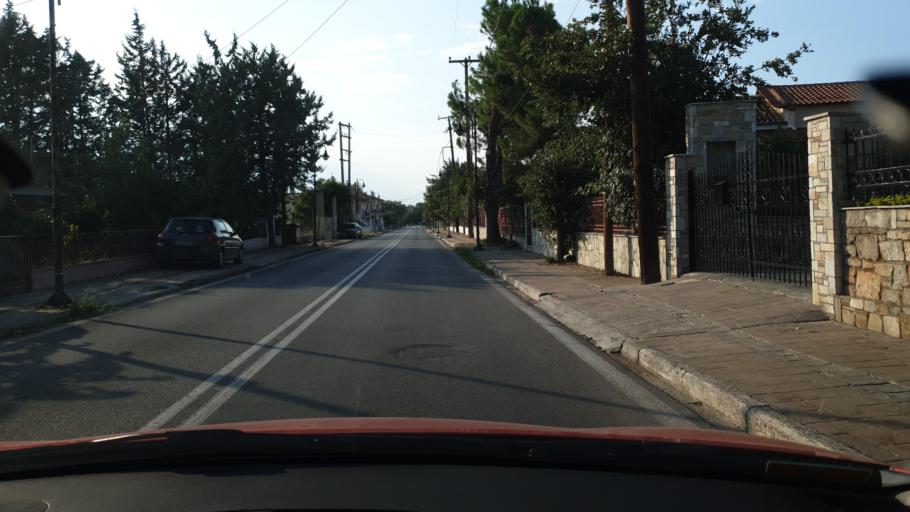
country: GR
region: Thessaly
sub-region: Nomos Magnisias
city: Sourpi
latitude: 39.0991
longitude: 22.8974
